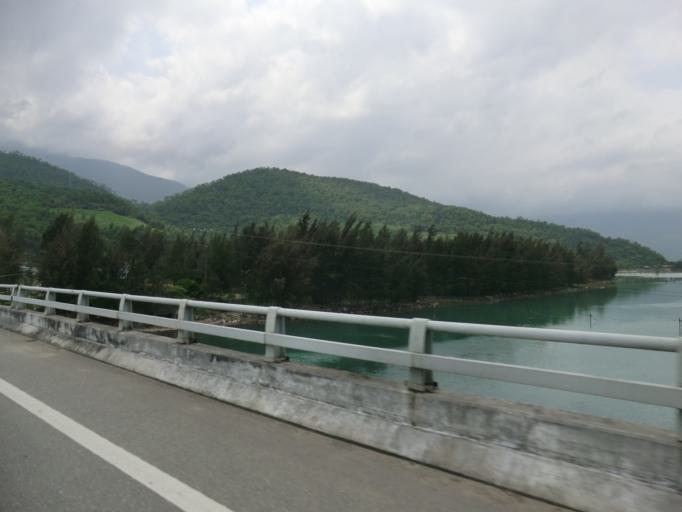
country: VN
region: Da Nang
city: Lien Chieu
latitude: 16.2251
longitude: 108.0829
